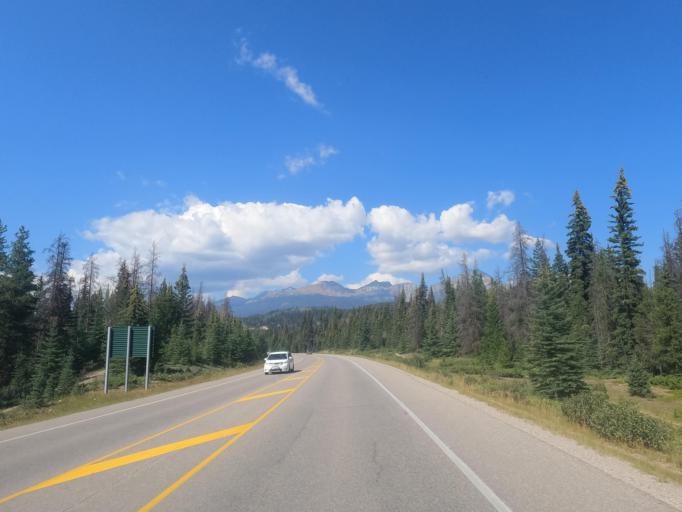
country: CA
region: Alberta
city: Jasper Park Lodge
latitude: 52.8602
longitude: -118.0812
